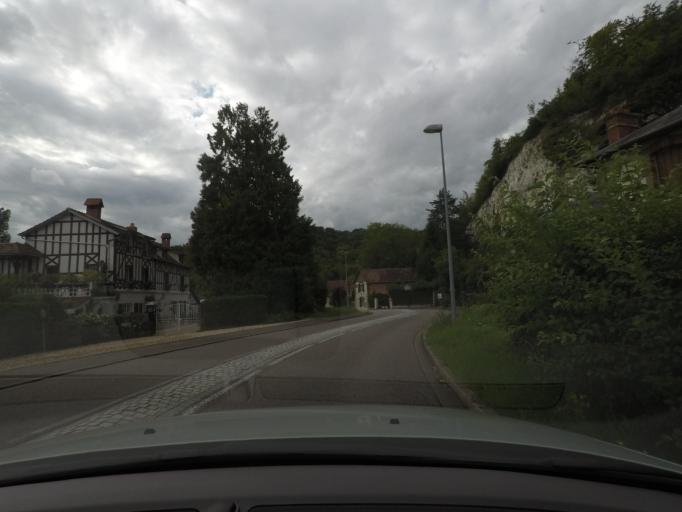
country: FR
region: Haute-Normandie
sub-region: Departement de l'Eure
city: Les Andelys
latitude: 49.2525
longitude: 1.3812
